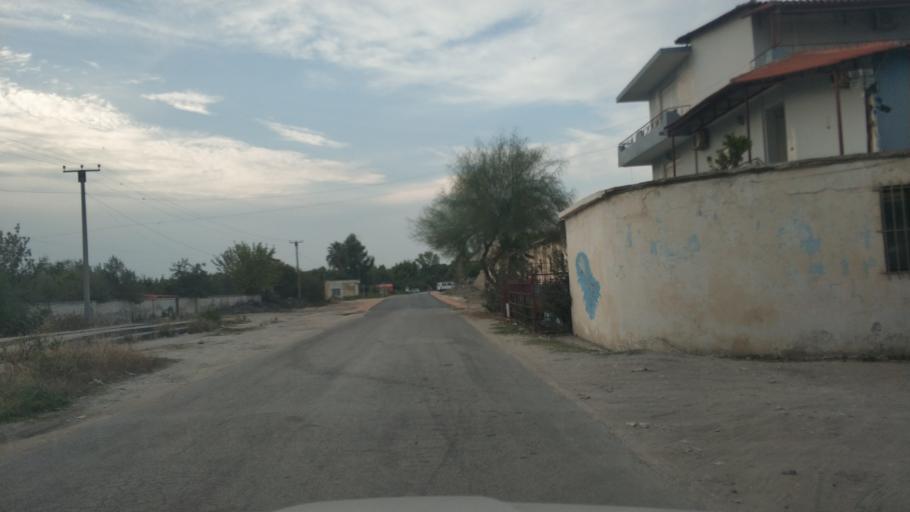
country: AL
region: Vlore
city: Vlore
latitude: 40.4759
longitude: 19.4539
